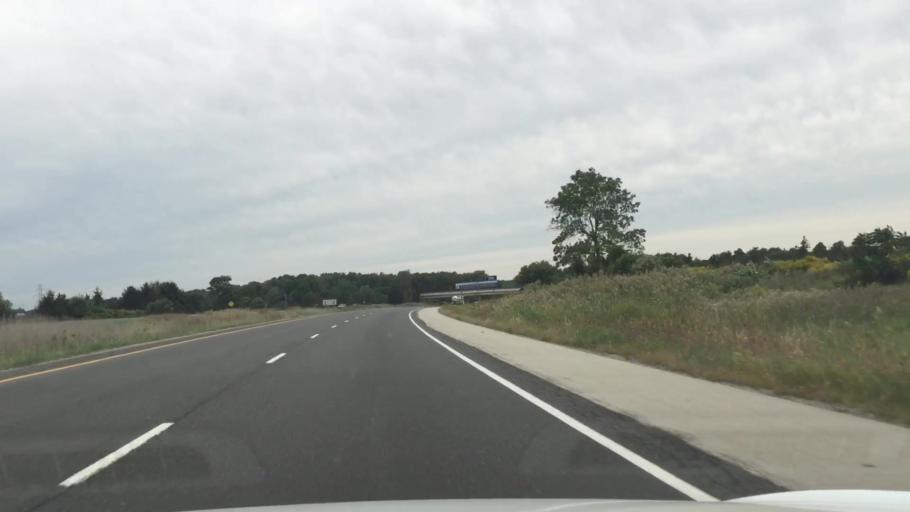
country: CA
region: Ontario
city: Delaware
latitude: 42.8941
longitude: -81.4159
